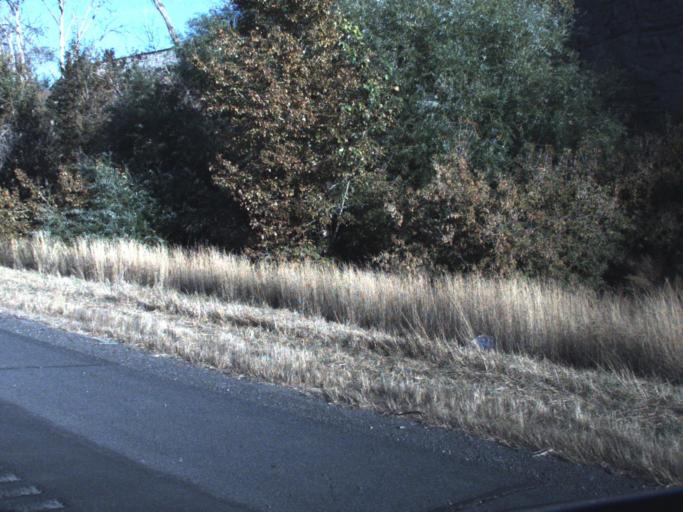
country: US
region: Washington
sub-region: Yakima County
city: Zillah
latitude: 46.3956
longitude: -120.2532
